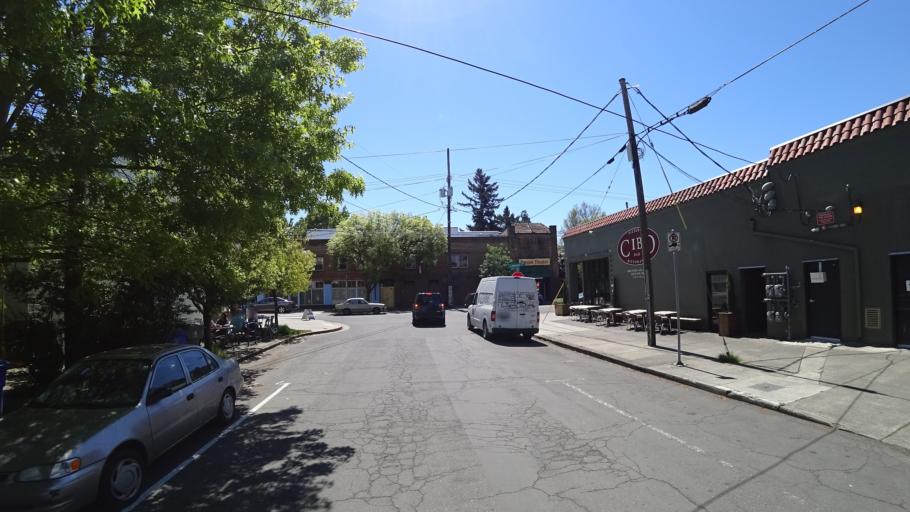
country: US
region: Oregon
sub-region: Multnomah County
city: Portland
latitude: 45.5051
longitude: -122.6276
